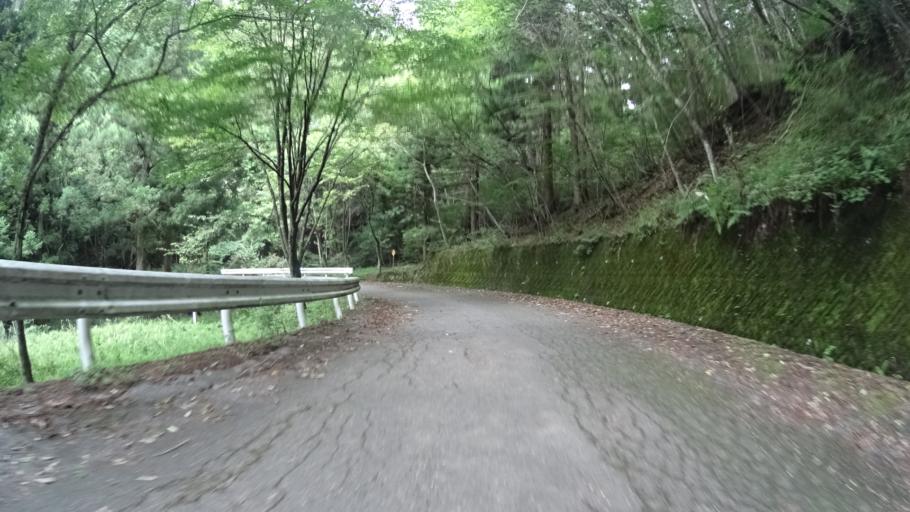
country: JP
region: Yamanashi
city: Kofu-shi
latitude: 35.8082
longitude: 138.5883
